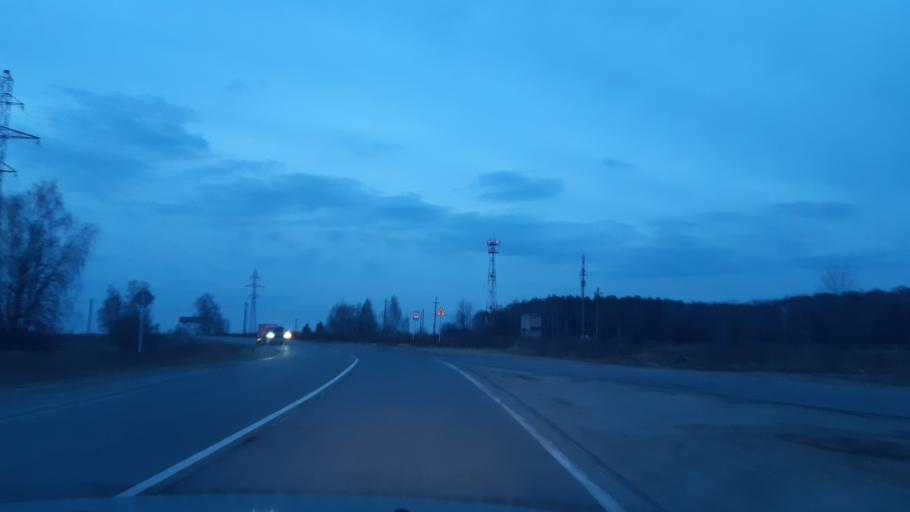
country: RU
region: Vladimir
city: Luknovo
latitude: 56.1980
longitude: 42.0337
